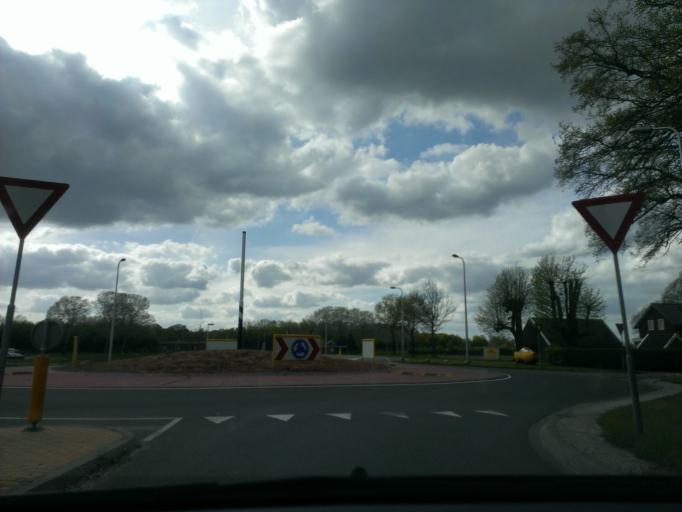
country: NL
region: Overijssel
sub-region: Gemeente Hof van Twente
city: Goor
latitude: 52.2944
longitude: 6.5595
